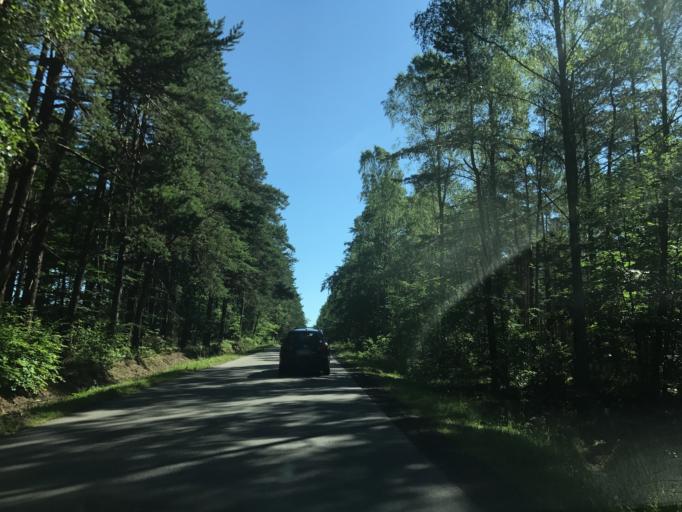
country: PL
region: Pomeranian Voivodeship
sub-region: Powiat bytowski
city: Czarna Dabrowka
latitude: 54.3392
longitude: 17.6527
